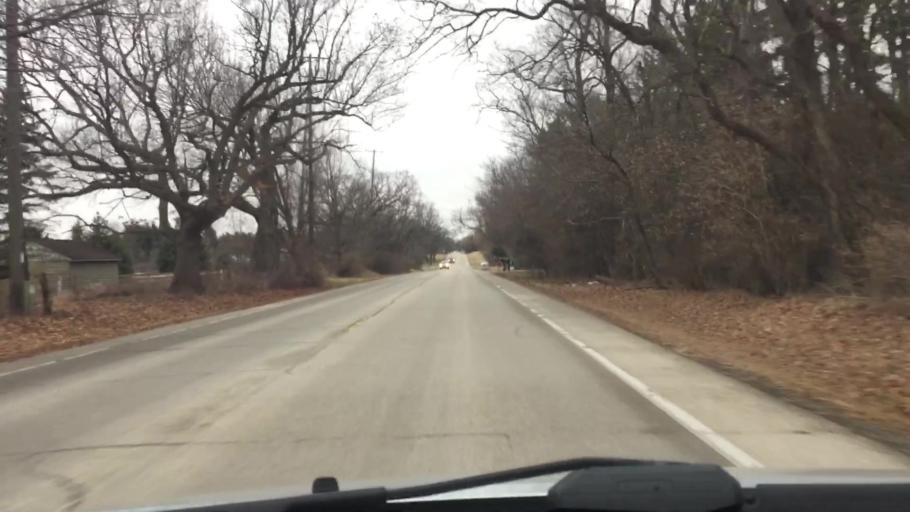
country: US
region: Wisconsin
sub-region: Waukesha County
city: Nashotah
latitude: 43.0813
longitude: -88.4034
